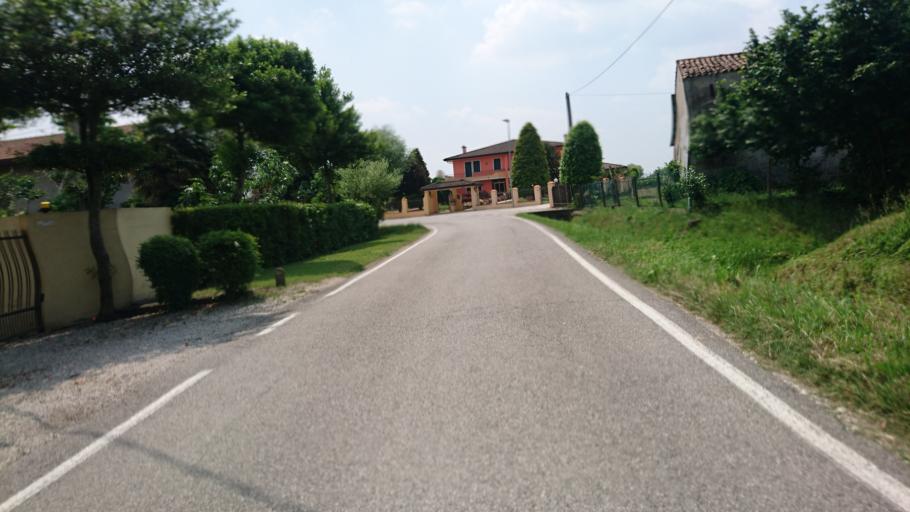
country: IT
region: Veneto
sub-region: Provincia di Padova
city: Cartura
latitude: 45.2629
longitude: 11.8810
